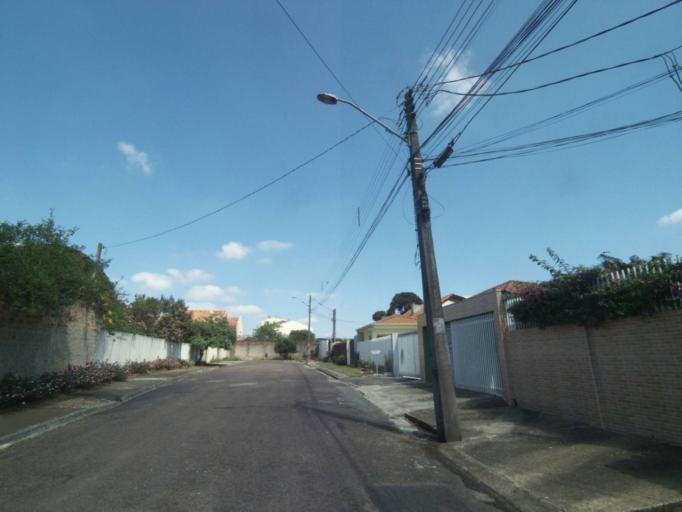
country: BR
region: Parana
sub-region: Sao Jose Dos Pinhais
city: Sao Jose dos Pinhais
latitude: -25.5201
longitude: -49.2382
